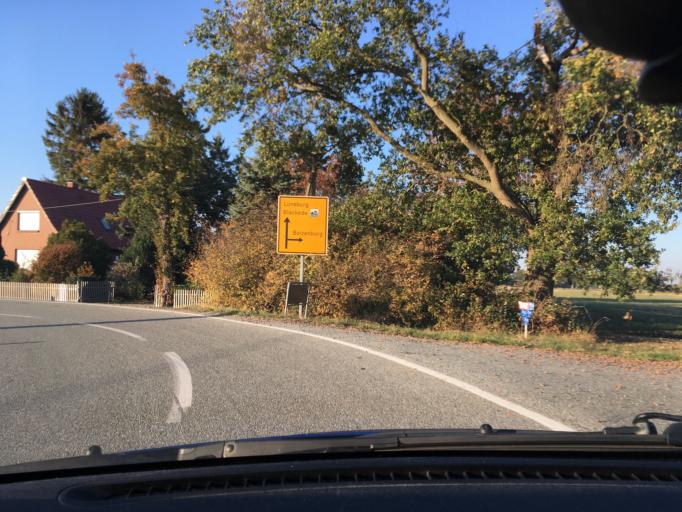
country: DE
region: Lower Saxony
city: Bleckede
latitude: 53.3034
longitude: 10.7883
